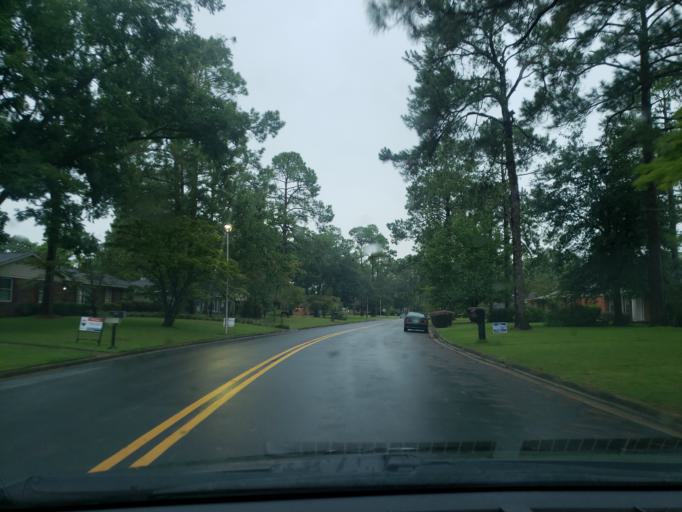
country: US
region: Georgia
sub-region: Dougherty County
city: Albany
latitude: 31.5963
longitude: -84.2055
